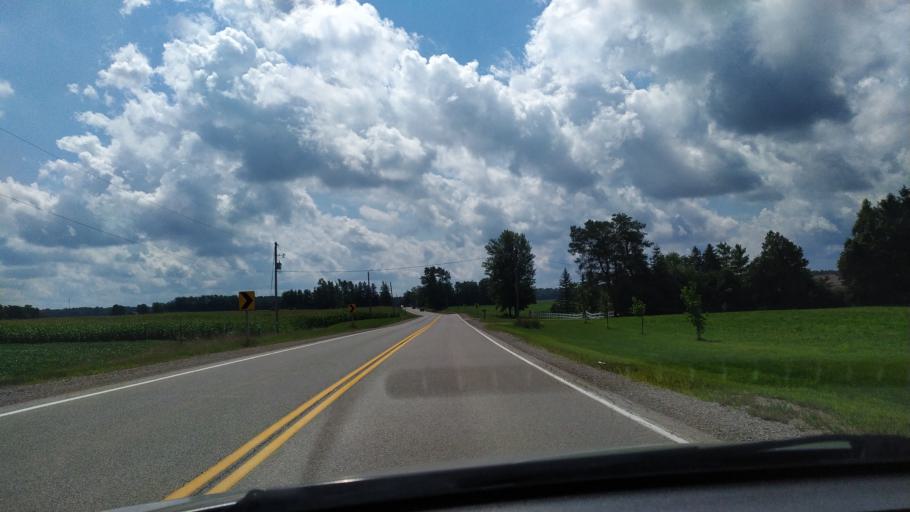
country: CA
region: Ontario
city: London
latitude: 43.0607
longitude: -81.3323
